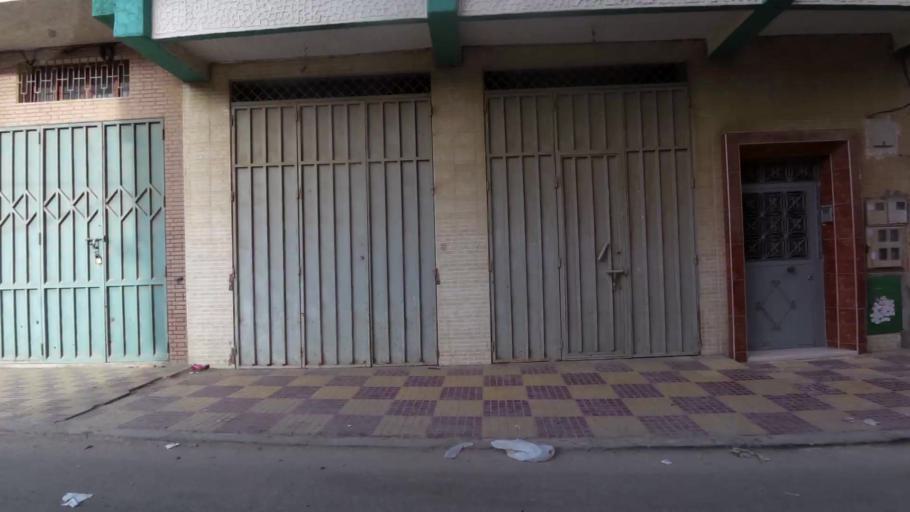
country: MA
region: Tanger-Tetouan
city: Tetouan
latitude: 35.5630
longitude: -5.3960
